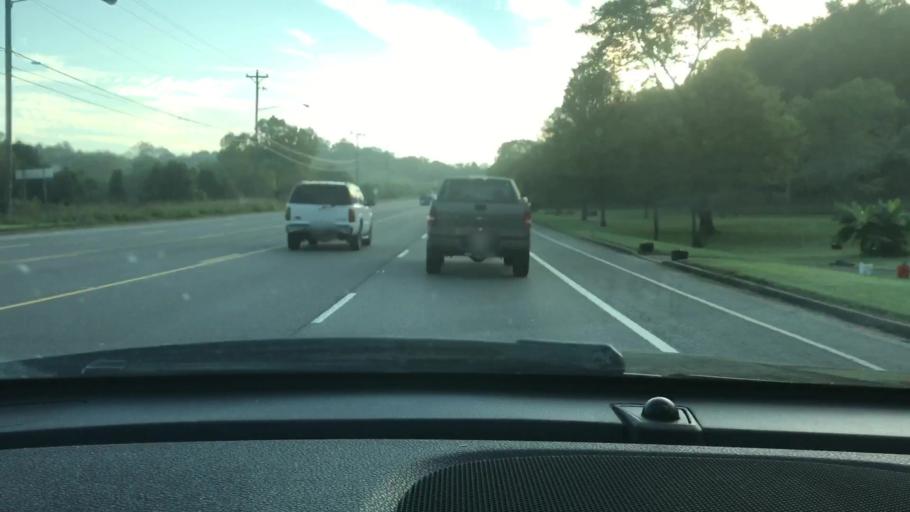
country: US
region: Tennessee
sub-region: Davidson County
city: Belle Meade
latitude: 36.2114
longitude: -86.9195
